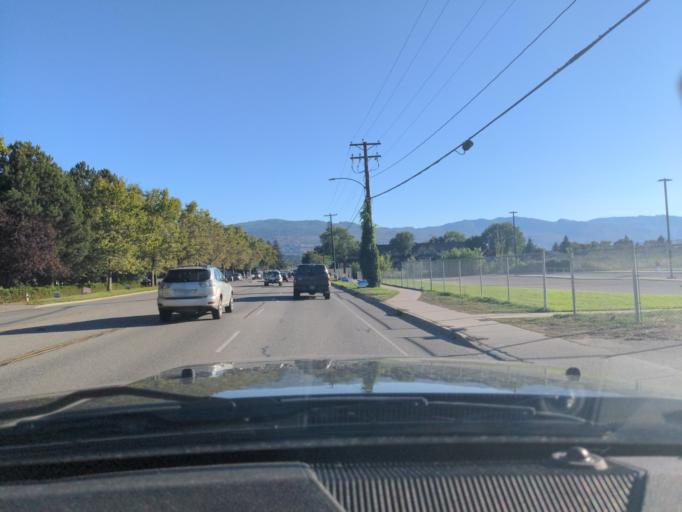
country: CA
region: British Columbia
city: Kelowna
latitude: 49.8600
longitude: -119.4745
